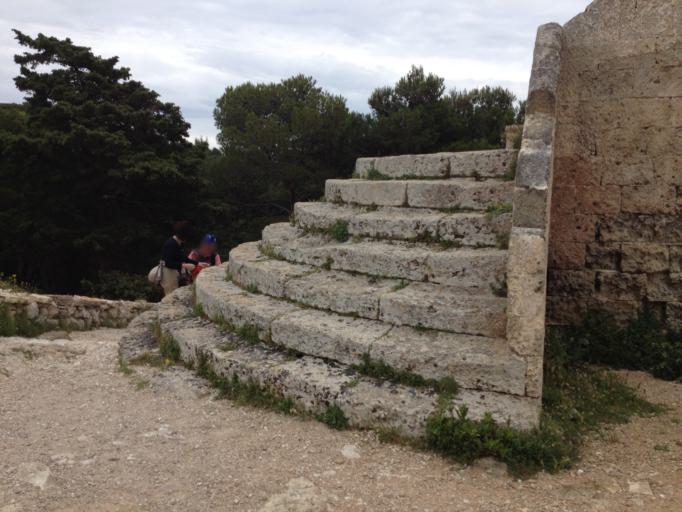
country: IT
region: Apulia
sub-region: Provincia di Lecce
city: Nardo
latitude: 40.1431
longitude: 17.9769
